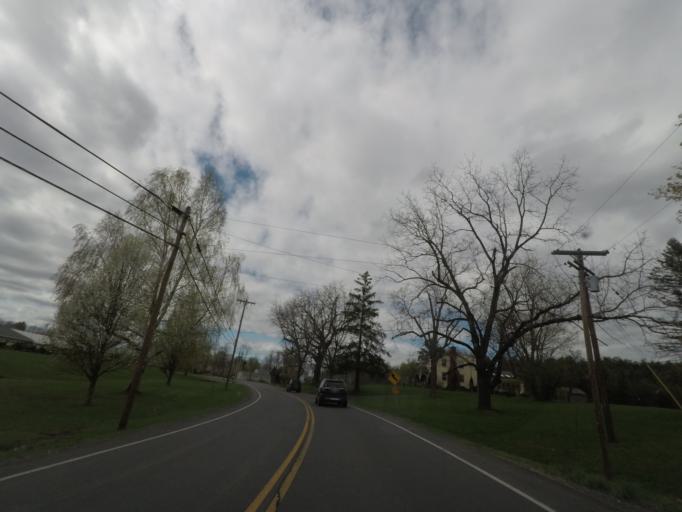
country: US
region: New York
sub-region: Columbia County
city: Chatham
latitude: 42.3722
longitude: -73.6220
